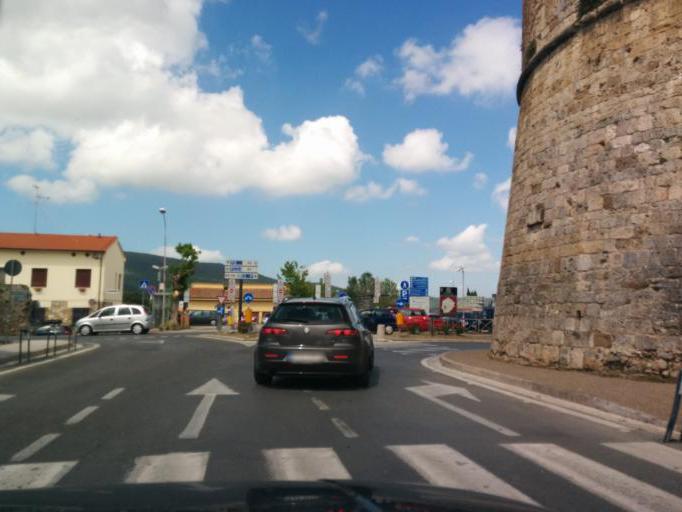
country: IT
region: Tuscany
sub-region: Provincia di Siena
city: San Gimignano
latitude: 43.4645
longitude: 11.0421
